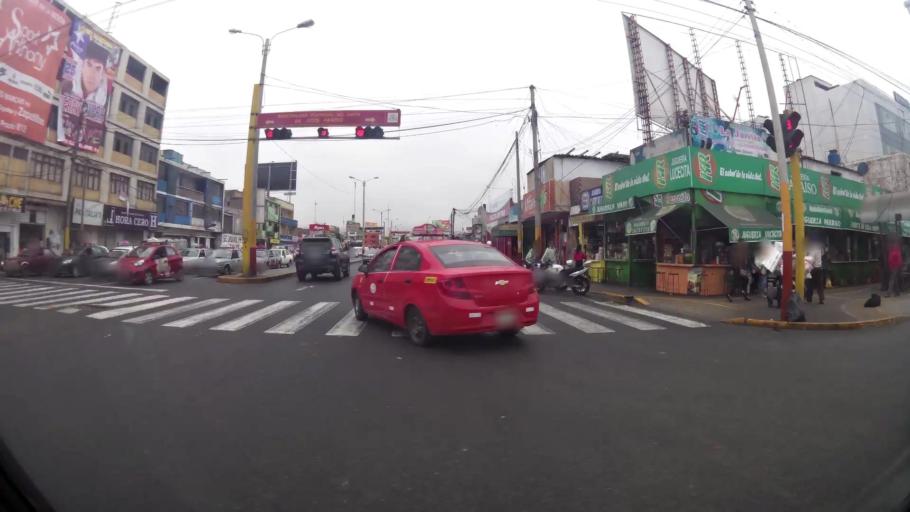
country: PE
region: Ancash
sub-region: Provincia de Santa
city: Chimbote
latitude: -9.0762
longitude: -78.5901
